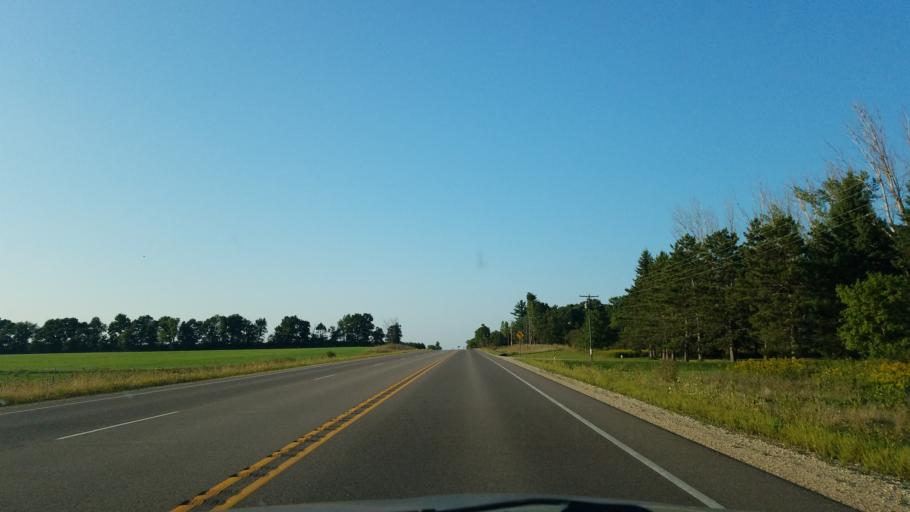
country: US
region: Wisconsin
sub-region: Saint Croix County
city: Baldwin
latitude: 45.1122
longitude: -92.3755
